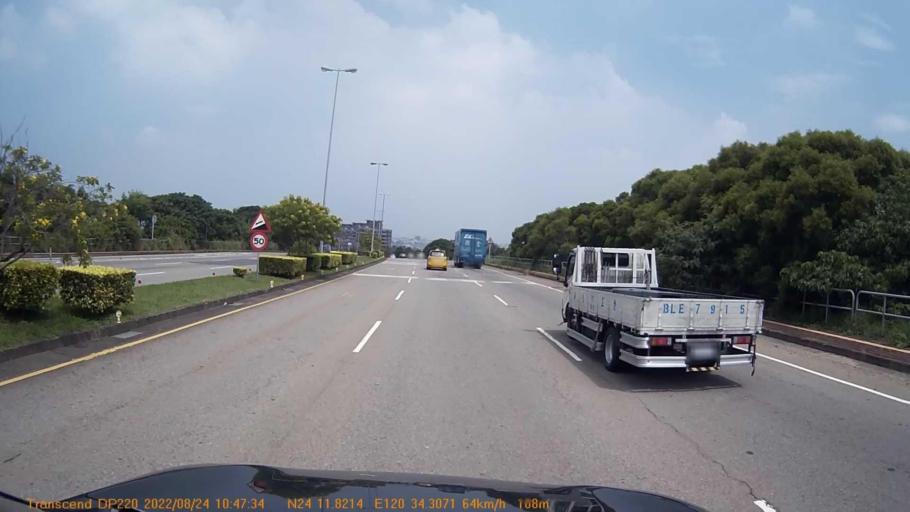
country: TW
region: Taiwan
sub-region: Taichung City
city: Taichung
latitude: 24.1973
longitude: 120.5716
